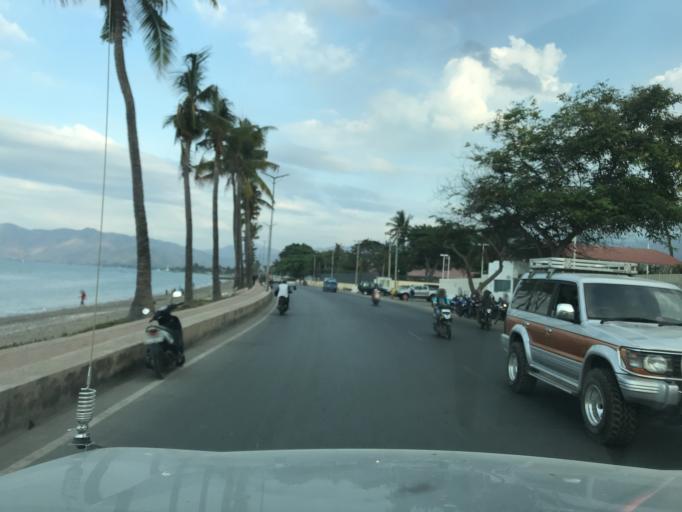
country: TL
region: Dili
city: Dili
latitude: -8.5454
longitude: 125.5503
